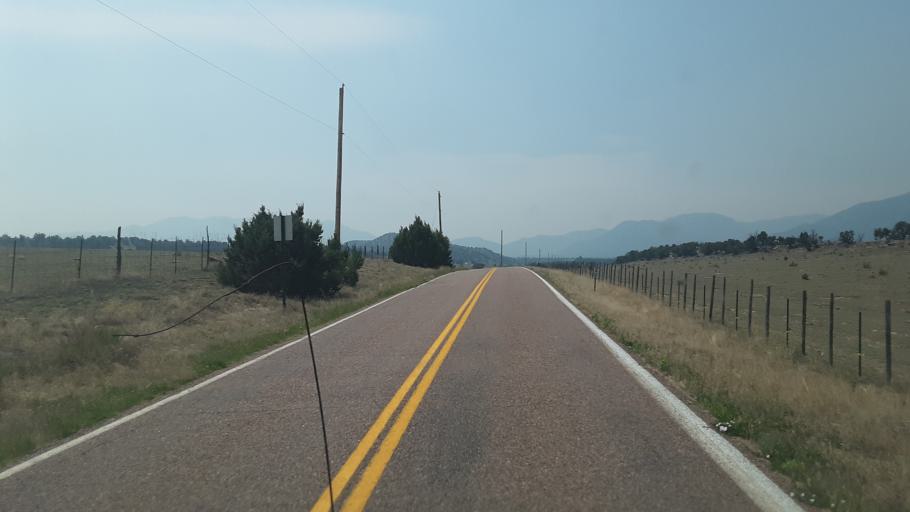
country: US
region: Colorado
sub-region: Fremont County
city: Canon City
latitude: 38.4588
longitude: -105.3757
